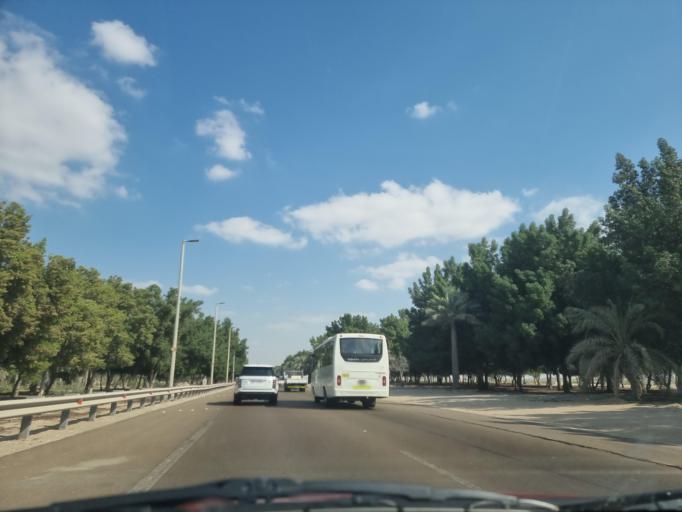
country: AE
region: Abu Dhabi
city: Abu Dhabi
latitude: 24.4089
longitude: 54.6316
